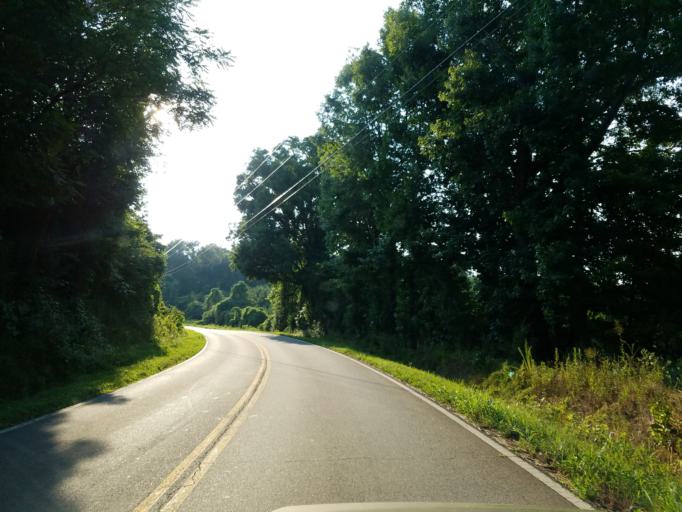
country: US
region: Georgia
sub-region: Pickens County
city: Jasper
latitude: 34.5402
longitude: -84.5362
